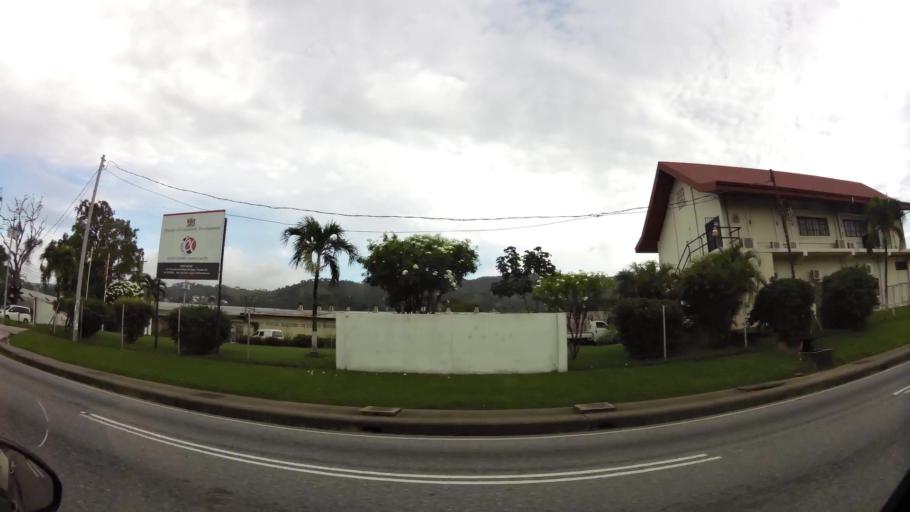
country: TT
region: Tunapuna/Piarco
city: Tunapuna
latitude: 10.6500
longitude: -61.4321
